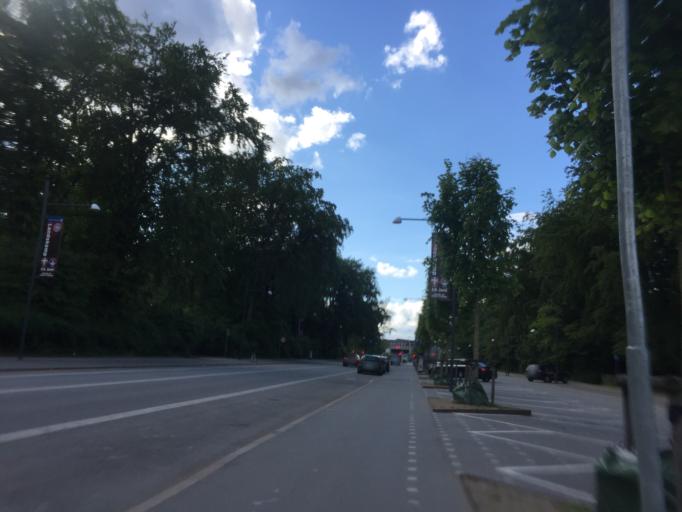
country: DK
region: Capital Region
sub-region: Kobenhavn
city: Copenhagen
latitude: 55.7036
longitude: 12.5682
